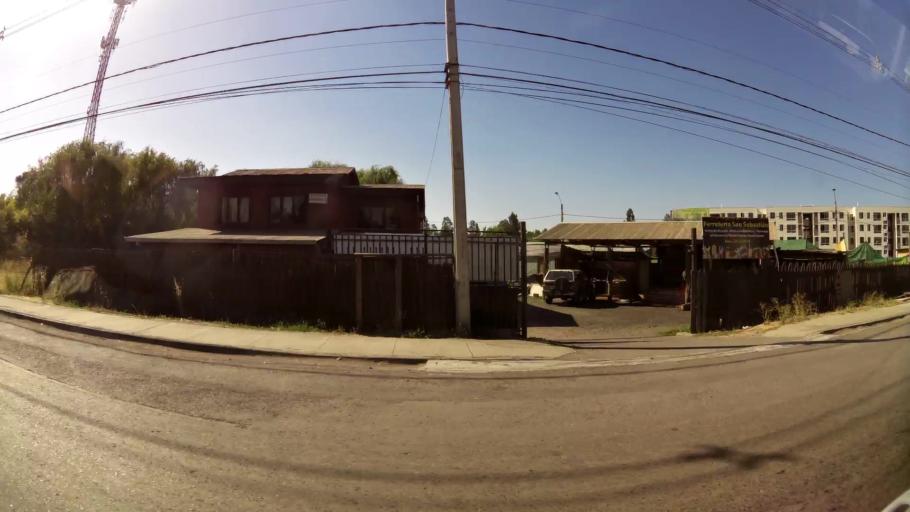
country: CL
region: Maule
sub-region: Provincia de Talca
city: Talca
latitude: -35.3998
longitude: -71.6289
